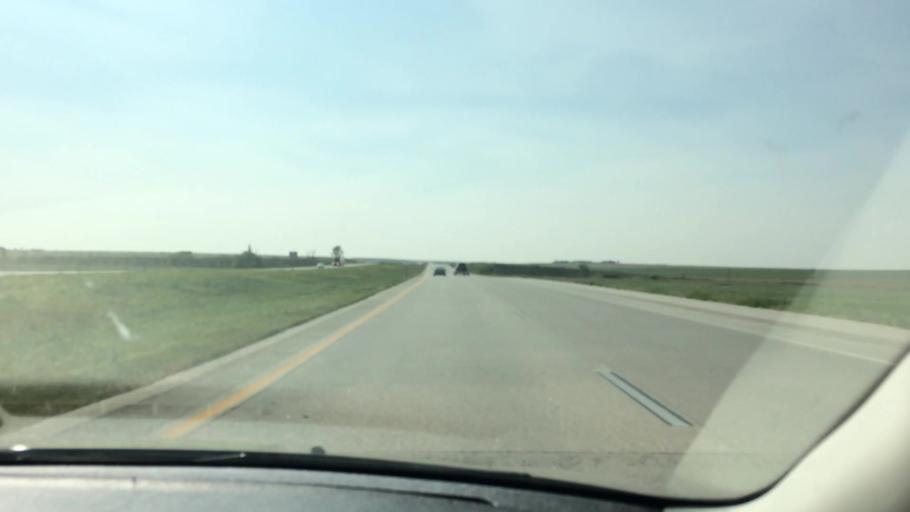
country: US
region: Colorado
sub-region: Arapahoe County
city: Byers
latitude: 39.7207
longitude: -104.2411
